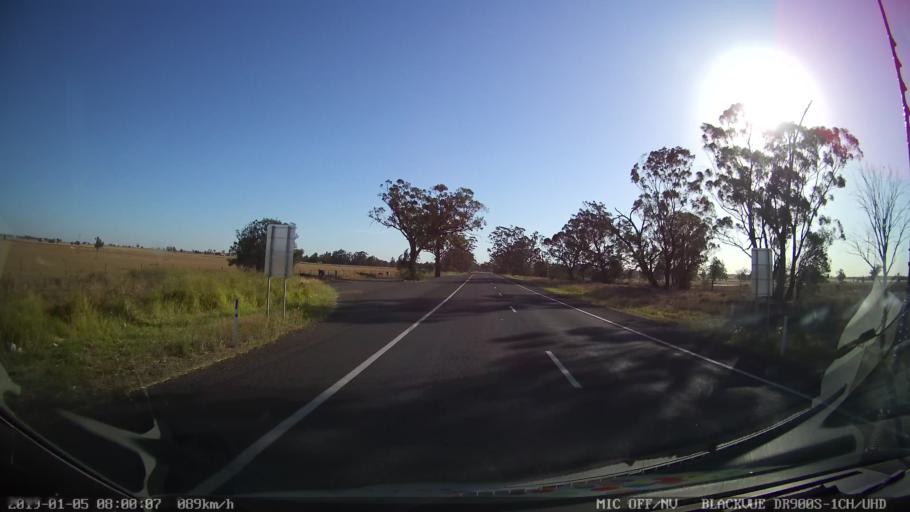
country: AU
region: New South Wales
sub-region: Gilgandra
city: Gilgandra
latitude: -31.6953
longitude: 148.6840
